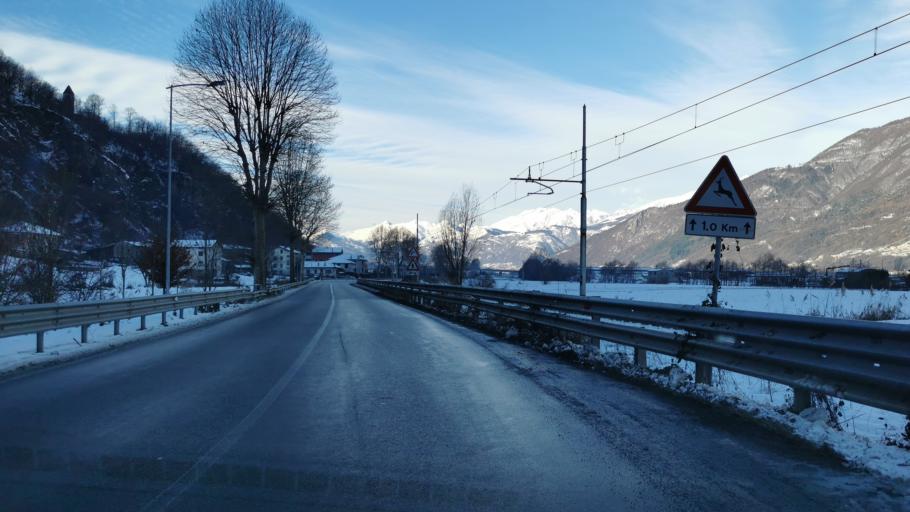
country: IT
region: Lombardy
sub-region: Provincia di Sondrio
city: Cercino
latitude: 46.1358
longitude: 9.5114
